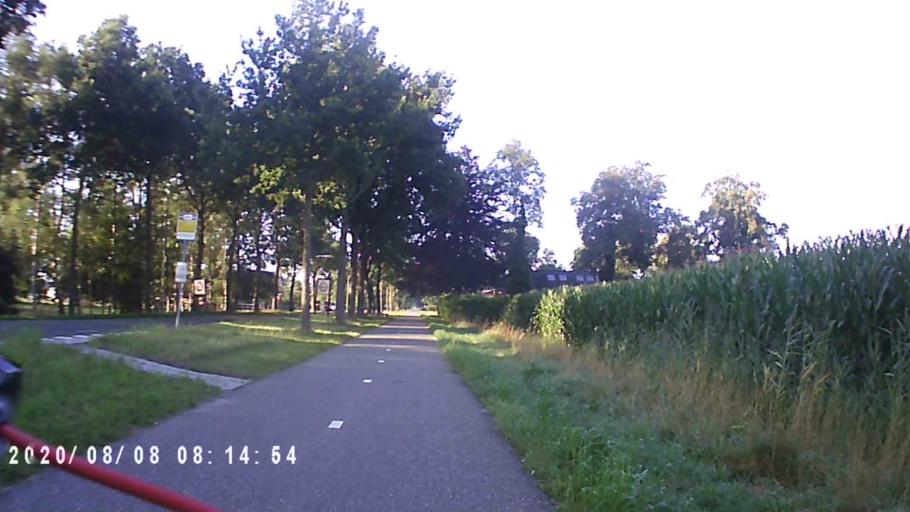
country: NL
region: Groningen
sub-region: Gemeente Leek
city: Leek
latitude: 53.0956
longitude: 6.3413
